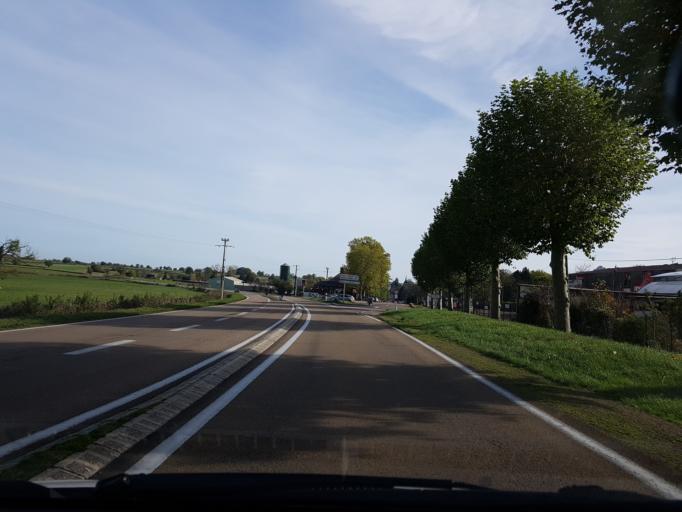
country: FR
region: Bourgogne
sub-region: Departement de l'Yonne
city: Avallon
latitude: 47.4749
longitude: 4.0172
